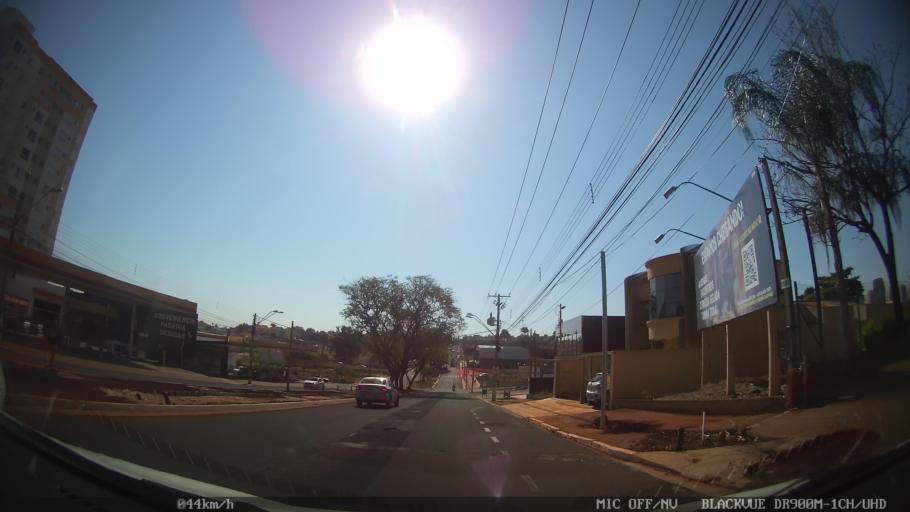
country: BR
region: Sao Paulo
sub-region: Ribeirao Preto
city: Ribeirao Preto
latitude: -21.2049
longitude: -47.8208
